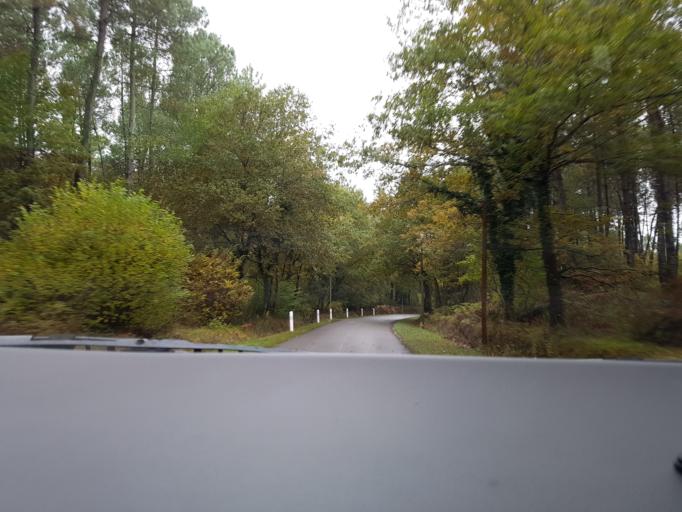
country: FR
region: Aquitaine
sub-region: Departement des Landes
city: Roquefort
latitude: 44.0513
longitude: -0.3419
